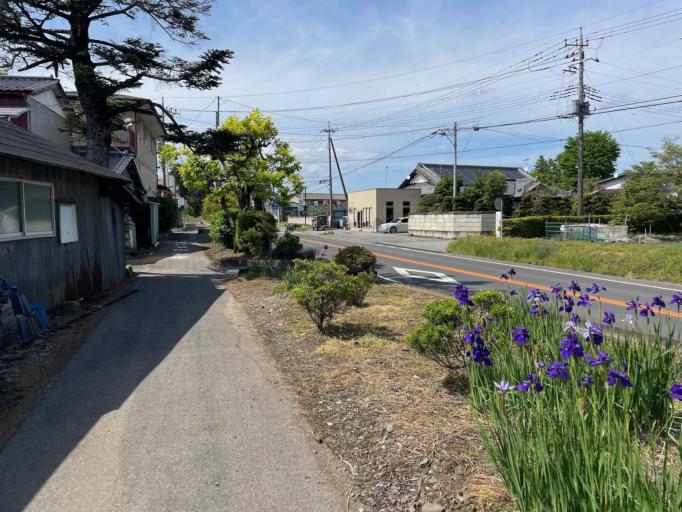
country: JP
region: Tochigi
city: Kanuma
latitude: 36.4857
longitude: 139.7607
